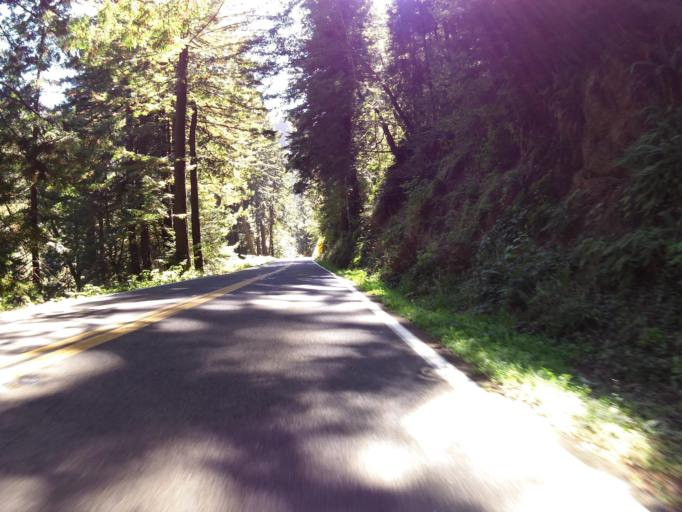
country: US
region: California
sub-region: Mendocino County
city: Fort Bragg
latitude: 39.7159
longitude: -123.8001
